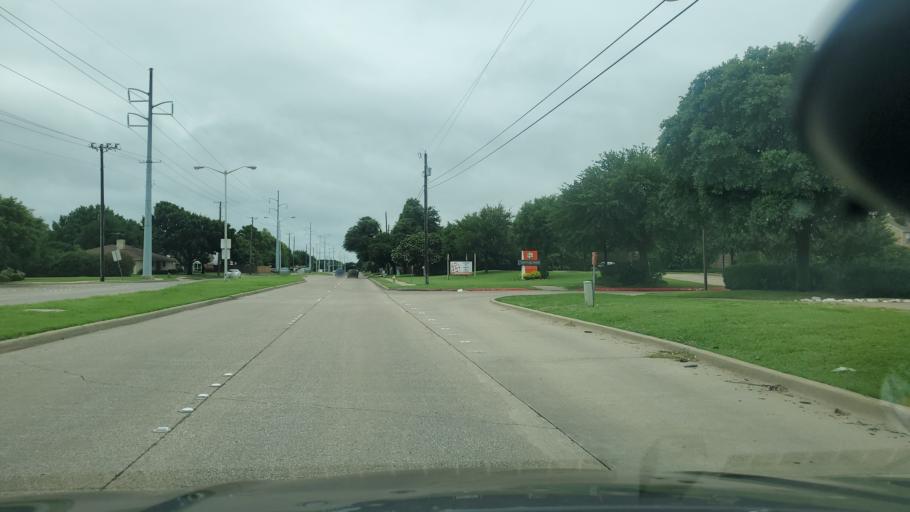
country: US
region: Texas
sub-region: Dallas County
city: Garland
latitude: 32.9442
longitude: -96.6653
